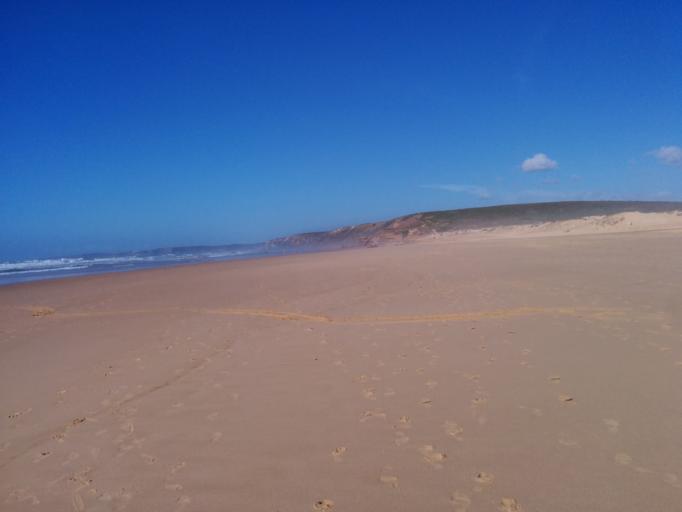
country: PT
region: Faro
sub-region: Vila do Bispo
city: Vila do Bispo
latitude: 37.2005
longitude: -8.9014
